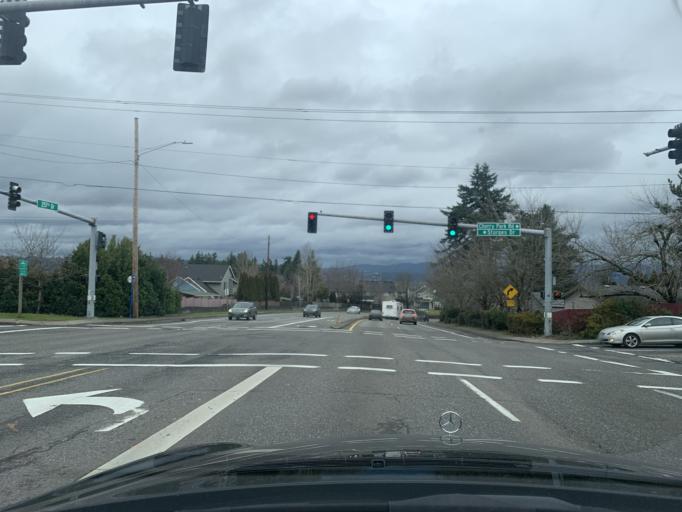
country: US
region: Oregon
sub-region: Multnomah County
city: Troutdale
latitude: 45.5334
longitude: -122.3993
